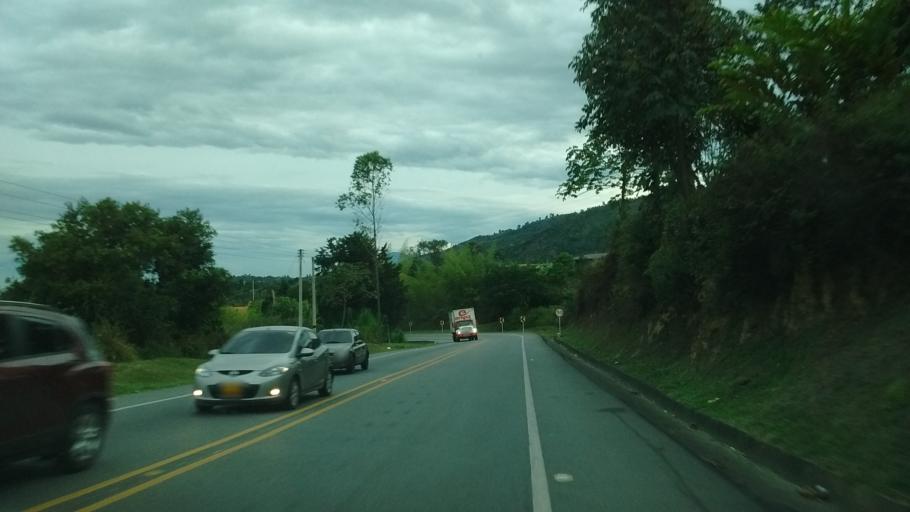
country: CO
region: Cauca
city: Morales
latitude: 2.7105
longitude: -76.5393
